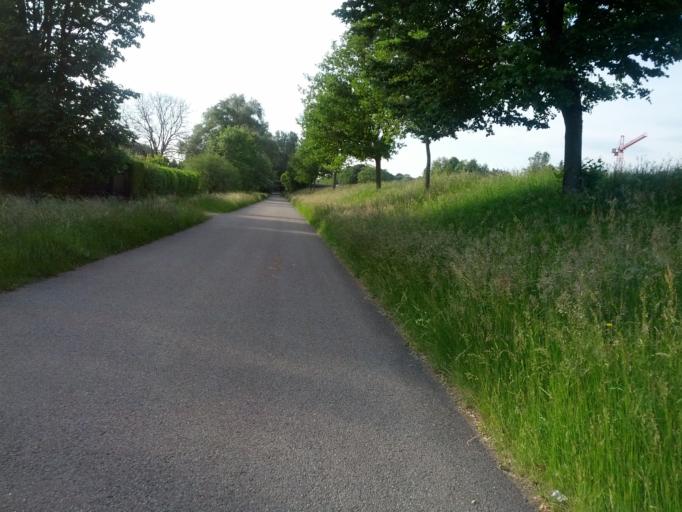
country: DE
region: Baden-Wuerttemberg
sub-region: Freiburg Region
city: Umkirch
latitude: 48.0246
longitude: 7.7922
